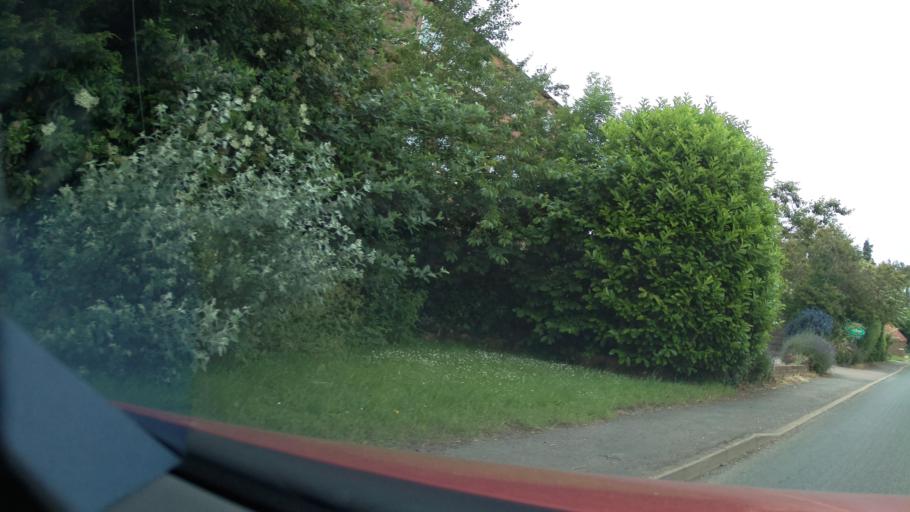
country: GB
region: England
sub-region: District of Rutland
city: Preston
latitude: 52.6120
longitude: -0.7130
